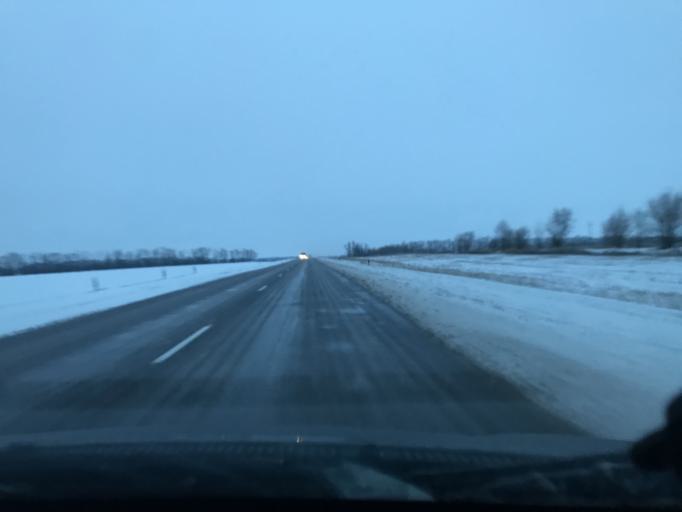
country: RU
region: Rostov
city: Letnik
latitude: 45.9813
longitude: 41.2403
